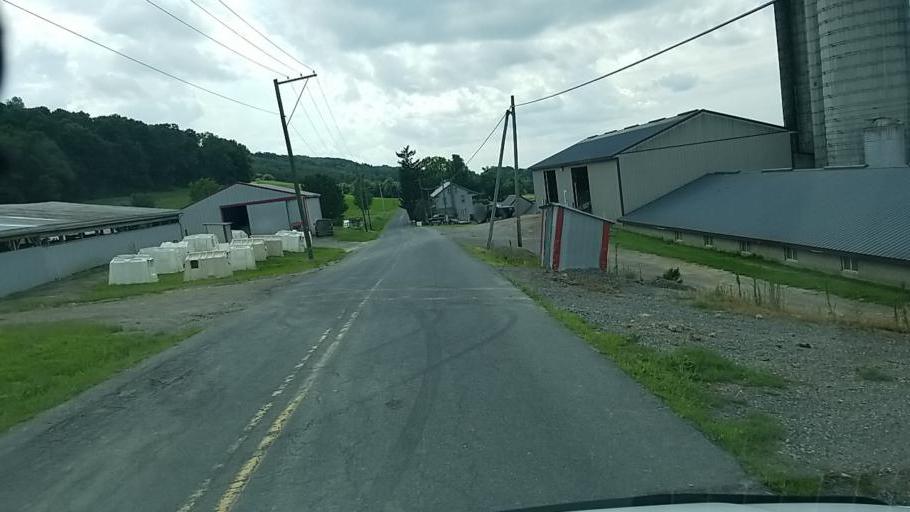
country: US
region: Pennsylvania
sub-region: Dauphin County
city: Elizabethville
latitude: 40.6600
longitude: -76.8423
